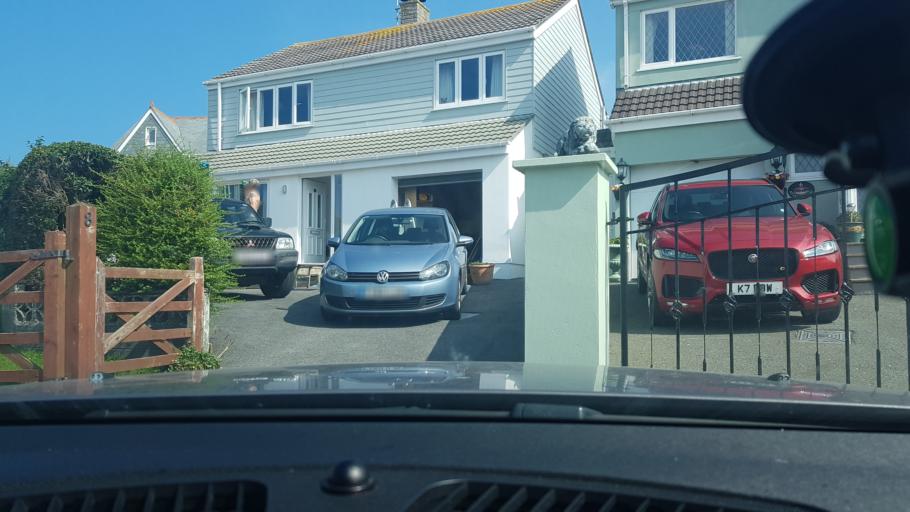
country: GB
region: England
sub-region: Cornwall
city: Tintagel
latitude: 50.6656
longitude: -4.7544
